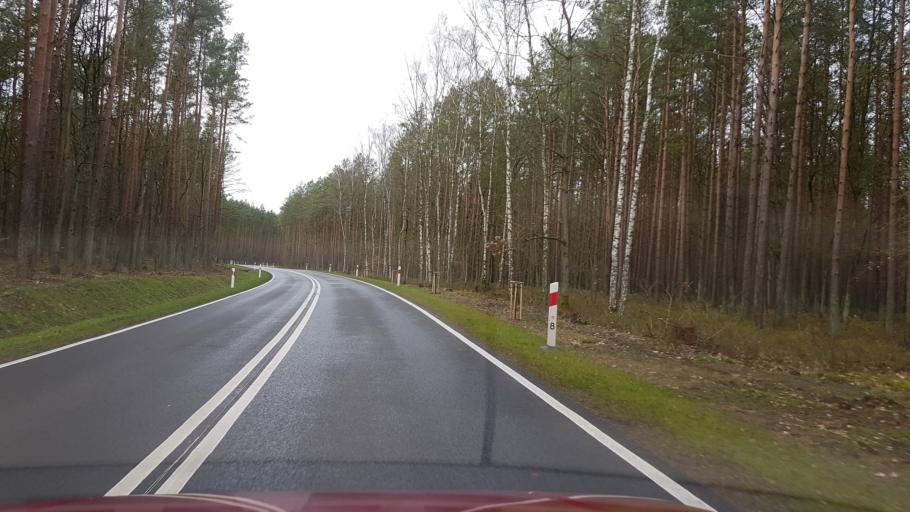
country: PL
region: West Pomeranian Voivodeship
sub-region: Powiat policki
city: Police
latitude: 53.6589
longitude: 14.4688
